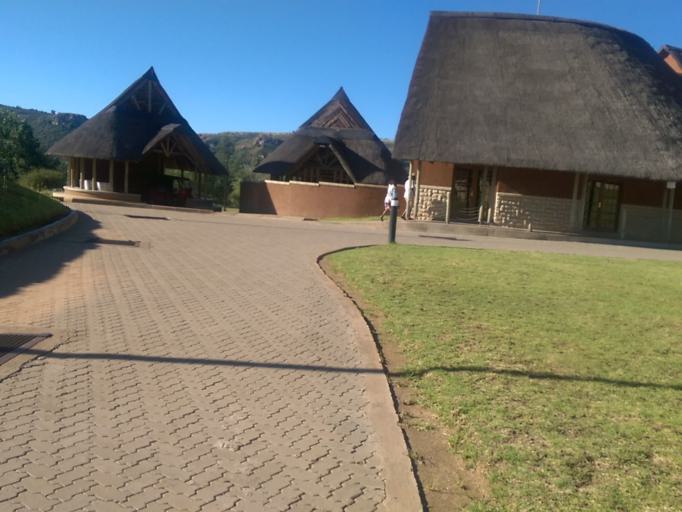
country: LS
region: Maseru
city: Maseru
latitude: -29.3455
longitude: 27.6619
